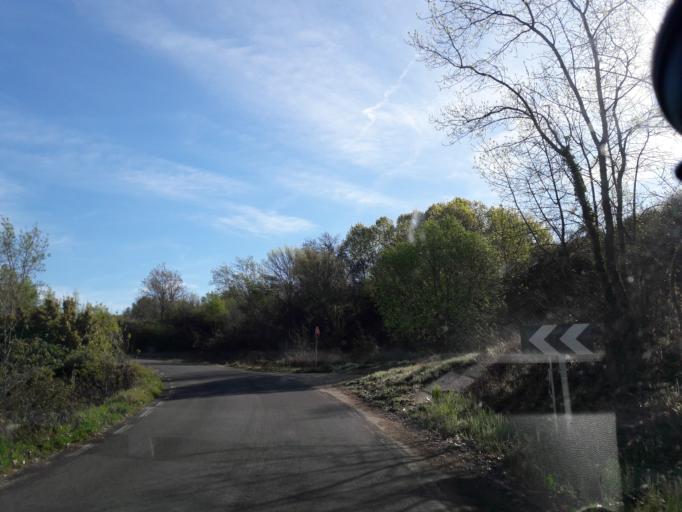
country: ES
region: Castille and Leon
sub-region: Provincia de Salamanca
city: Sanchotello
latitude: 40.4343
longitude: -5.7531
